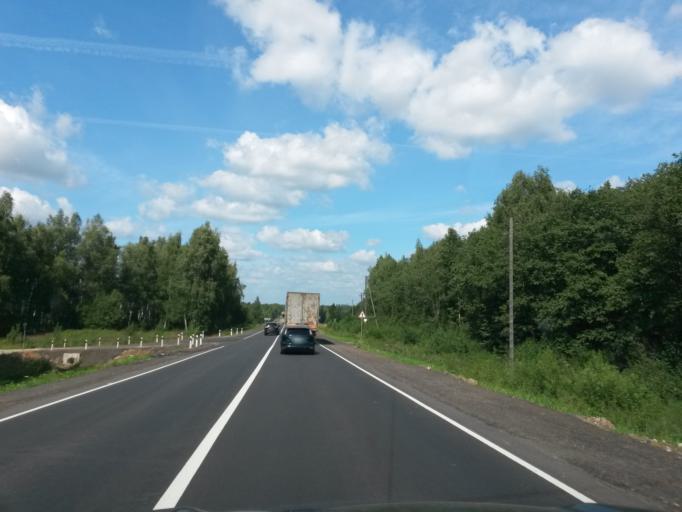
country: RU
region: Jaroslavl
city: Yaroslavl
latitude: 57.5046
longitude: 39.8986
